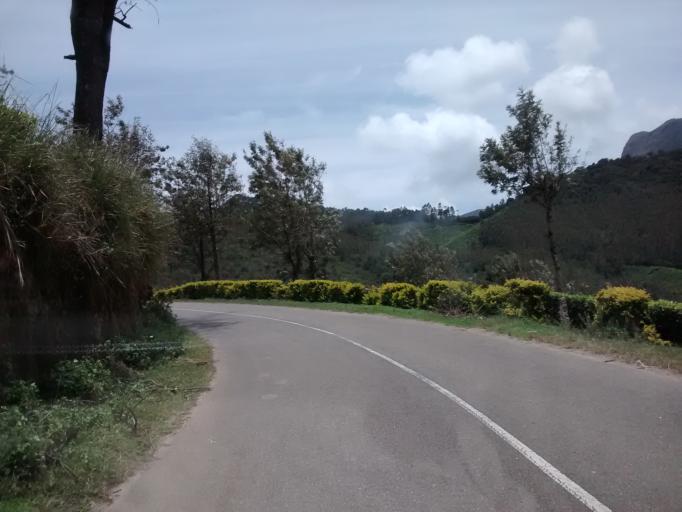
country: IN
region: Kerala
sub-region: Idukki
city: Munnar
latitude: 10.1301
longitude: 77.2115
